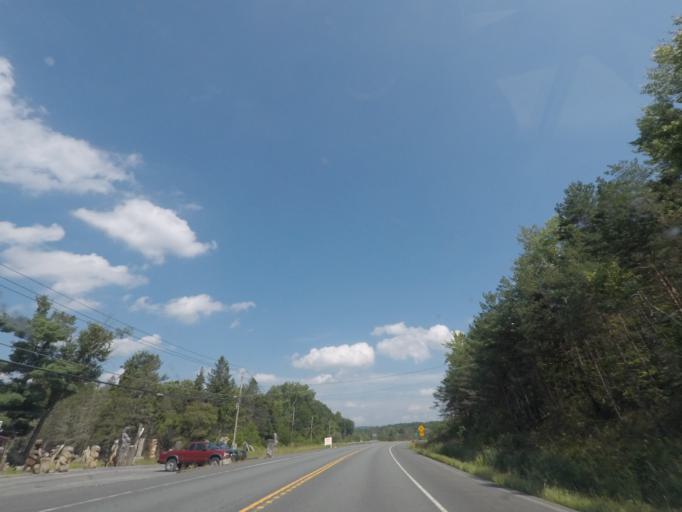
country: US
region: New York
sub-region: Rensselaer County
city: Hoosick Falls
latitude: 42.8463
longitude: -73.4676
